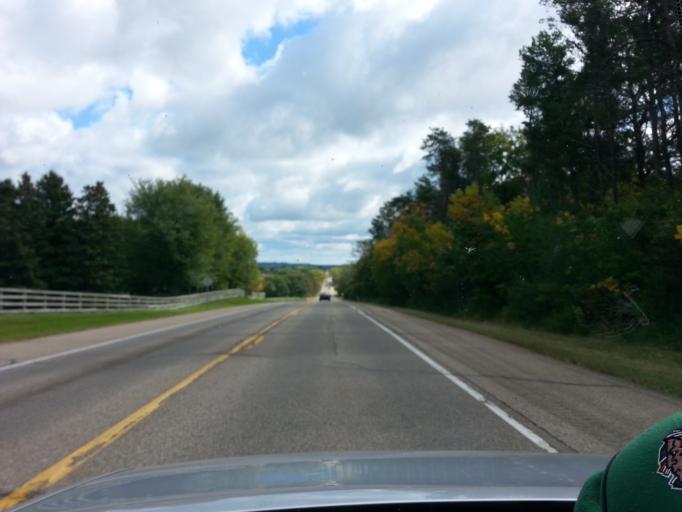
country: US
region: Minnesota
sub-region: Washington County
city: Oakdale
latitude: 44.9635
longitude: -92.9184
